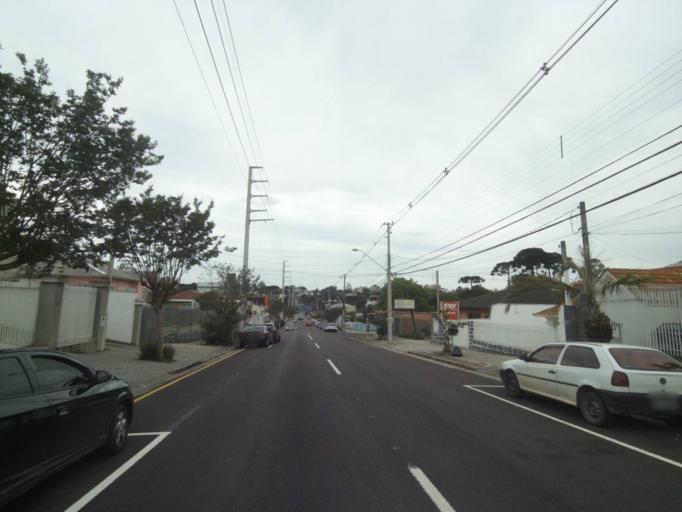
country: BR
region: Parana
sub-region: Curitiba
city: Curitiba
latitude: -25.4047
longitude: -49.2731
